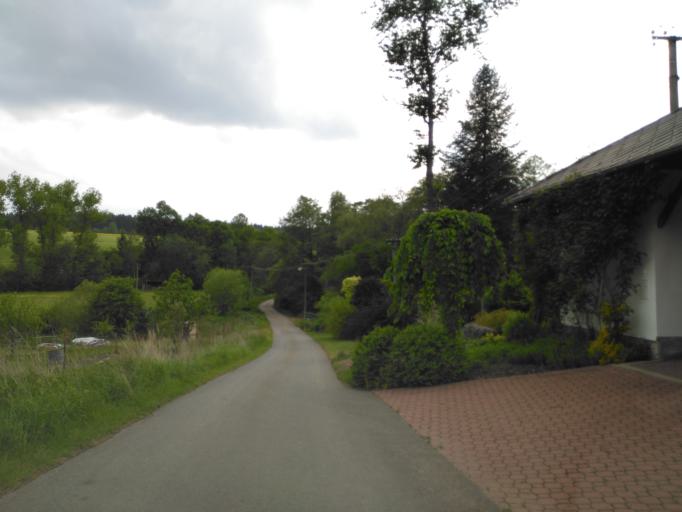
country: CZ
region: Plzensky
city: Zbiroh
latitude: 49.8575
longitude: 13.7286
